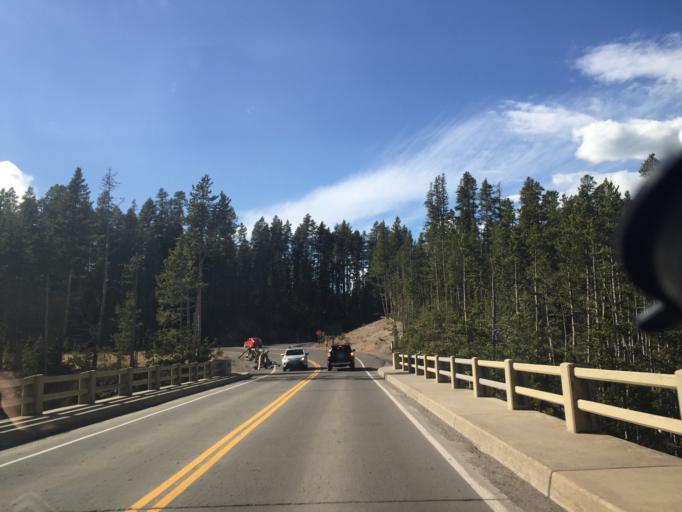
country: US
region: Montana
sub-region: Gallatin County
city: West Yellowstone
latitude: 44.7081
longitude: -110.5025
